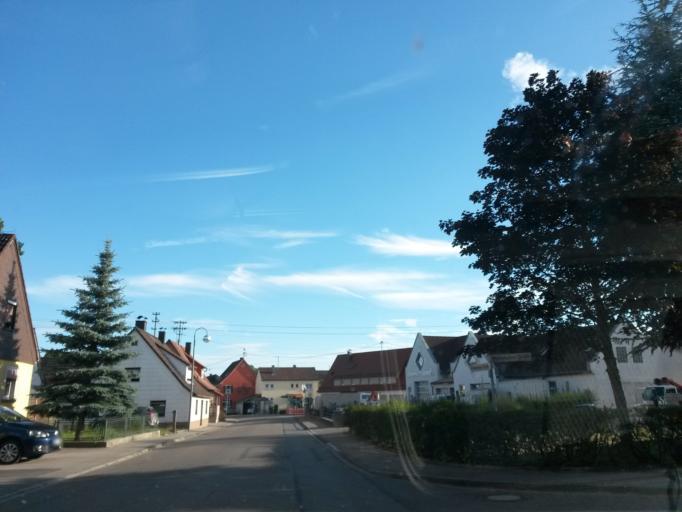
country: DE
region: Baden-Wuerttemberg
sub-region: Regierungsbezirk Stuttgart
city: Ellenberg
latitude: 49.0561
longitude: 10.2024
